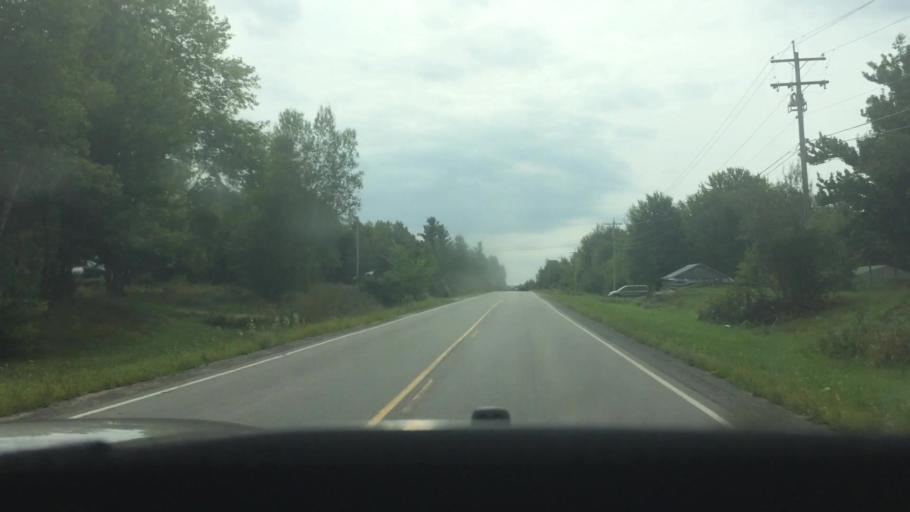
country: US
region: New York
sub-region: St. Lawrence County
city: Canton
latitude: 44.5008
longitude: -75.2683
